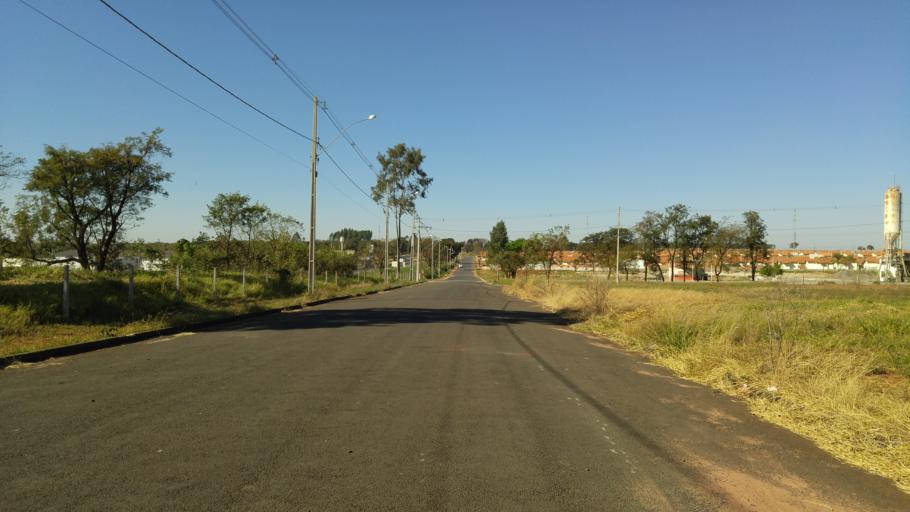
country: BR
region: Sao Paulo
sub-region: Paraguacu Paulista
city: Paraguacu Paulista
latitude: -22.4404
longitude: -50.5855
